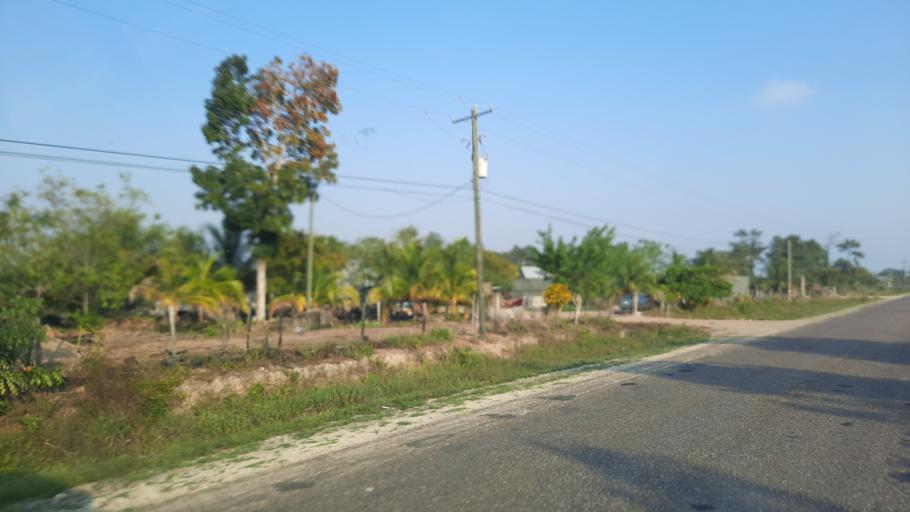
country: BZ
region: Stann Creek
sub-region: Dangriga
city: Dangriga
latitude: 16.8944
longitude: -88.3392
